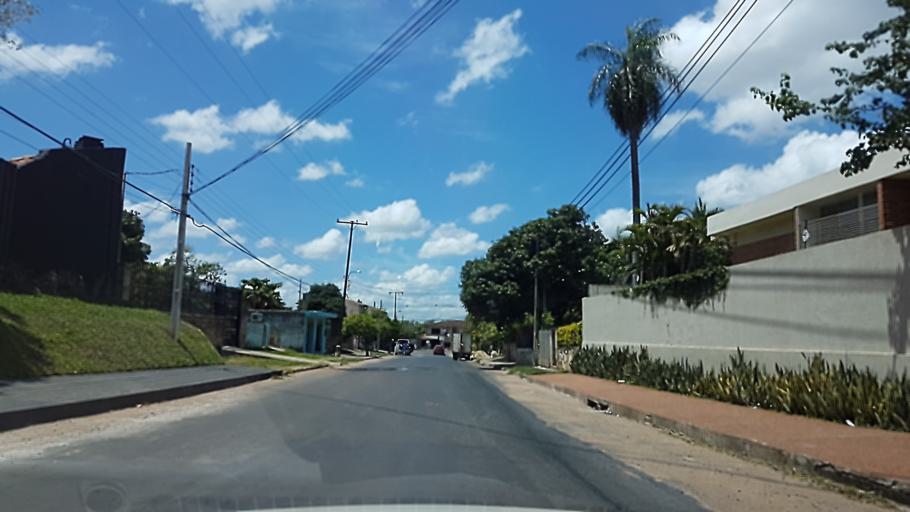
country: PY
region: Central
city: Colonia Mariano Roque Alonso
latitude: -25.2461
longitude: -57.5344
